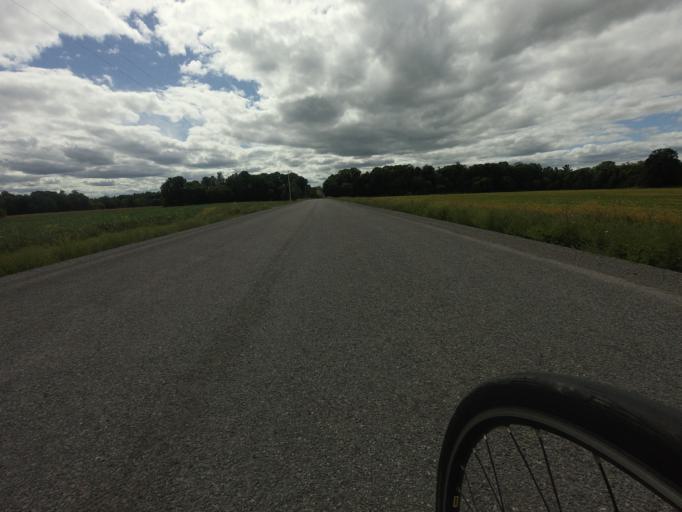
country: CA
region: Ontario
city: Carleton Place
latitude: 45.3108
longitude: -76.1980
